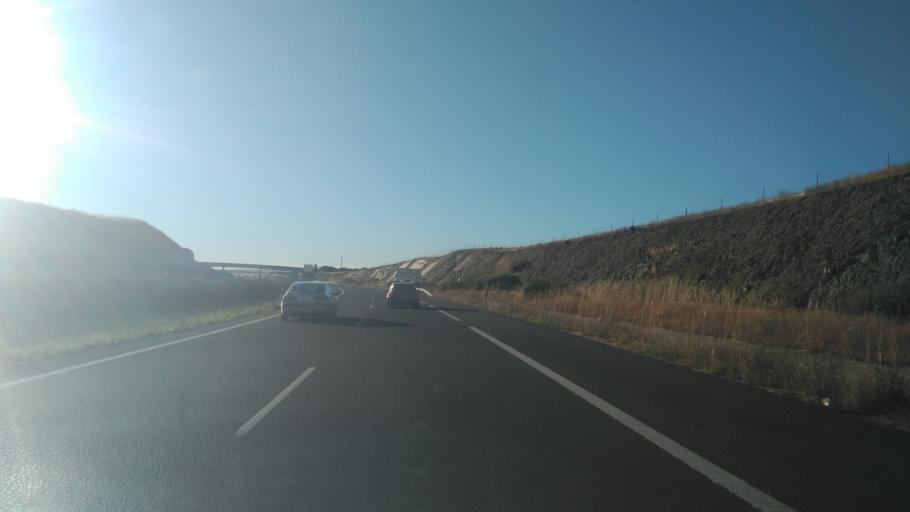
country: ES
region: Castille and Leon
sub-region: Provincia de Salamanca
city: Mozarbez
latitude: 40.8637
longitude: -5.6452
